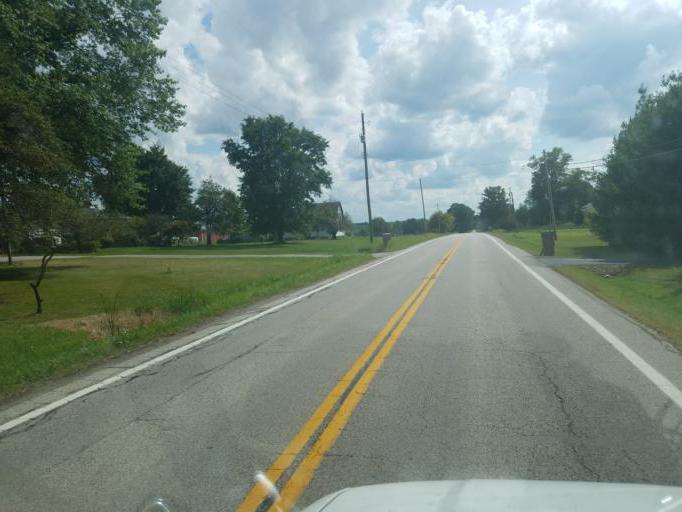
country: US
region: Ohio
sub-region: Portage County
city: Hiram
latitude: 41.3527
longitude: -81.1432
